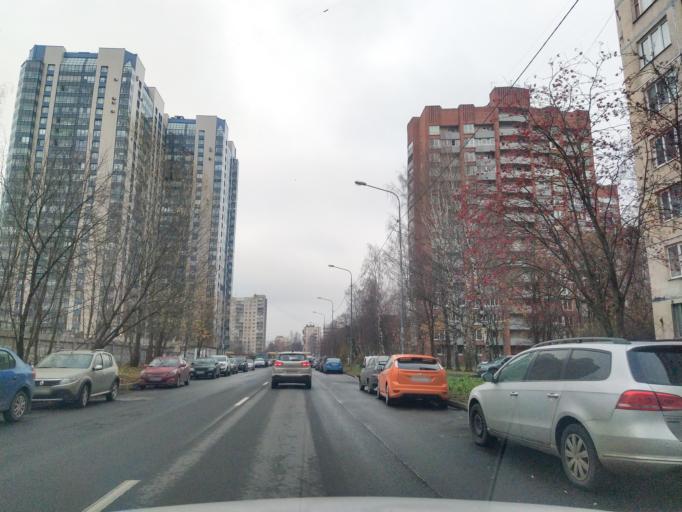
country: RU
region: Leningrad
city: Parnas
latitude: 60.0439
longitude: 30.3675
